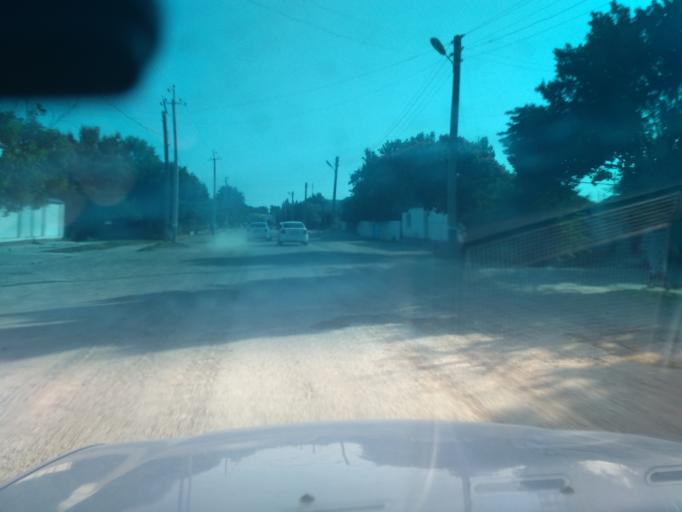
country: UZ
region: Sirdaryo
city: Guliston
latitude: 40.5347
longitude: 69.0385
